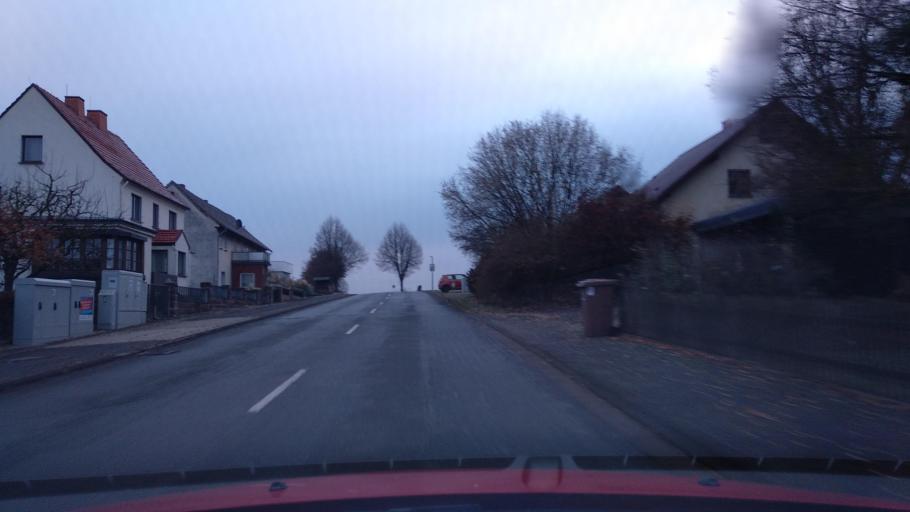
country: DE
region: Hesse
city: Liebenau
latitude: 51.4391
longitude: 9.3062
